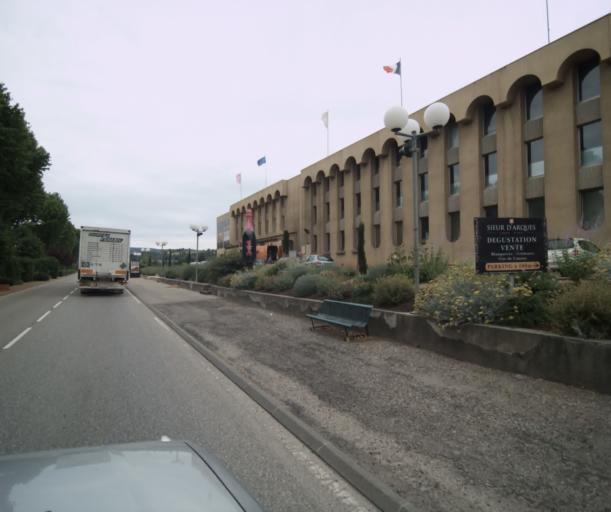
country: FR
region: Languedoc-Roussillon
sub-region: Departement de l'Aude
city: Limoux
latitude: 43.0715
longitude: 2.2194
